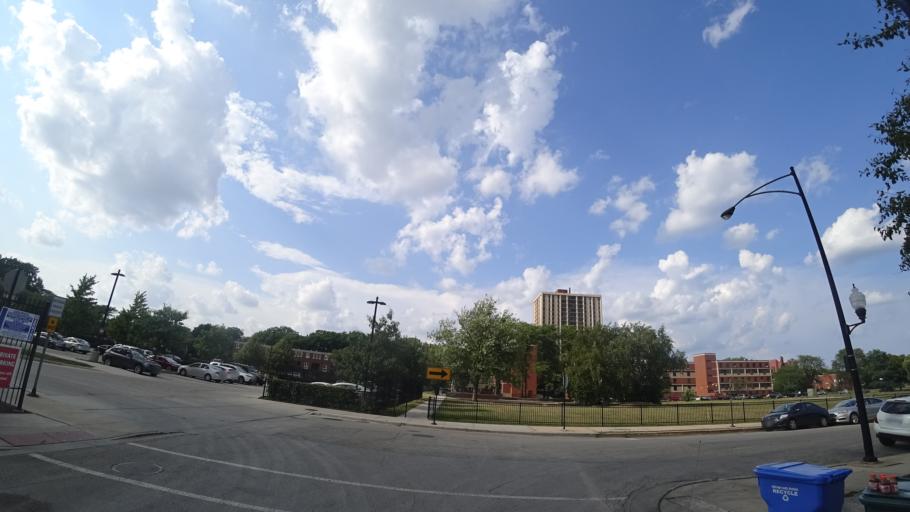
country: US
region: Illinois
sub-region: Cook County
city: Chicago
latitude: 41.8418
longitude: -87.6220
